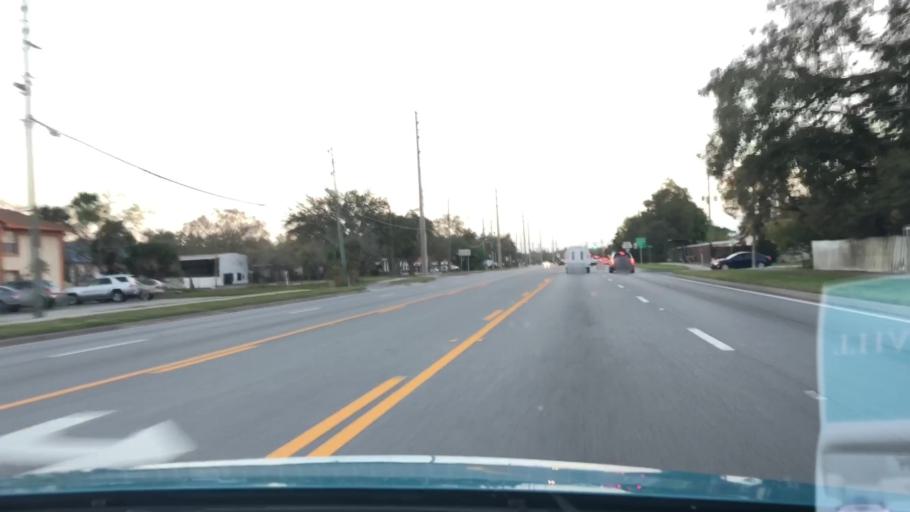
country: US
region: Florida
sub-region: Osceola County
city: Kissimmee
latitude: 28.3074
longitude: -81.3914
